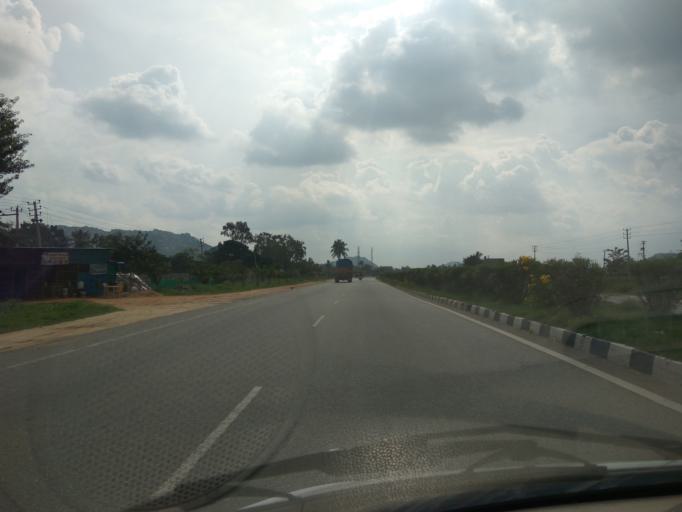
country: IN
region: Karnataka
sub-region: Kolar
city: Kolar
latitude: 13.1201
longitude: 78.0934
